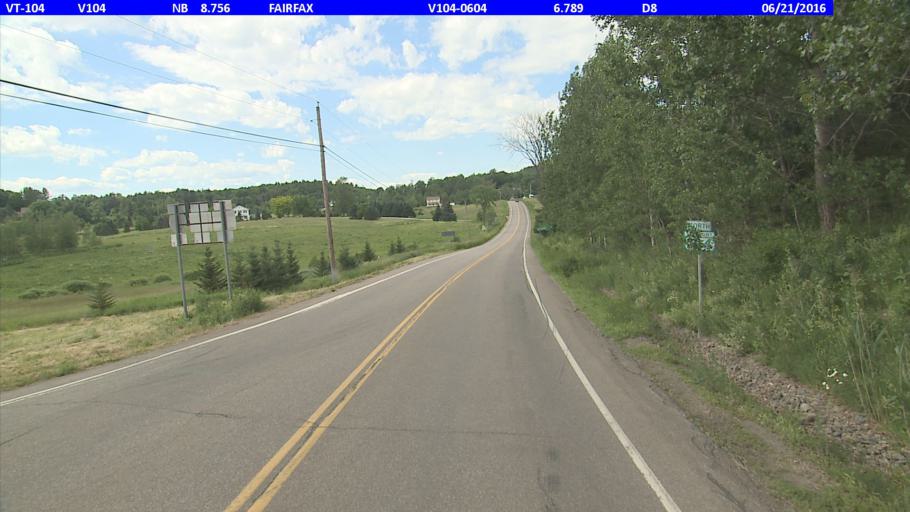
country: US
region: Vermont
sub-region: Chittenden County
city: Milton
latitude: 44.6832
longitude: -73.0296
